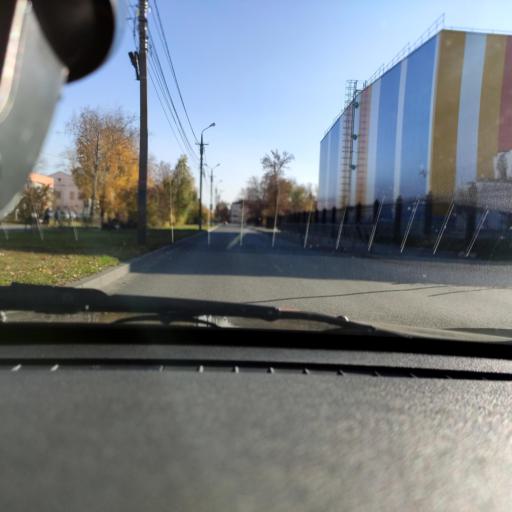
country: RU
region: Samara
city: Tol'yatti
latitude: 53.5158
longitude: 49.4078
